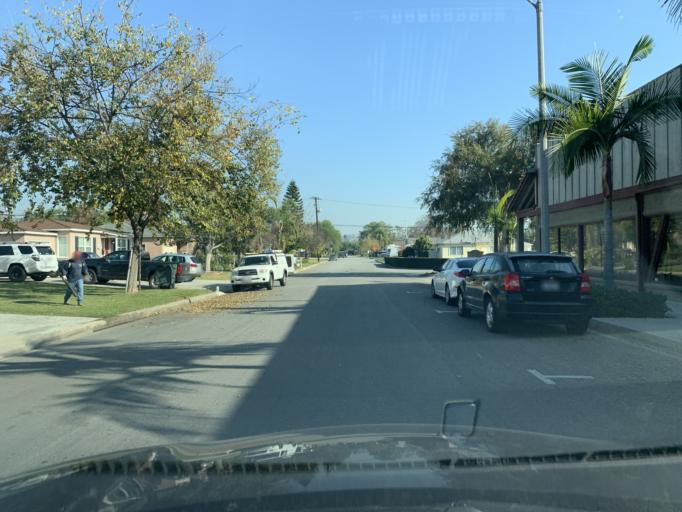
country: US
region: California
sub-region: Los Angeles County
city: Covina
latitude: 34.0768
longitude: -117.8890
